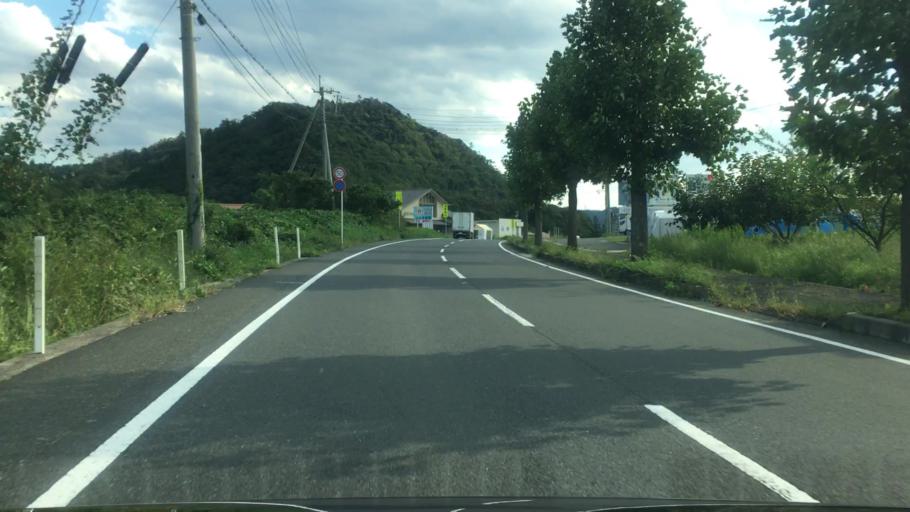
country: JP
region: Hyogo
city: Toyooka
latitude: 35.6233
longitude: 134.9285
